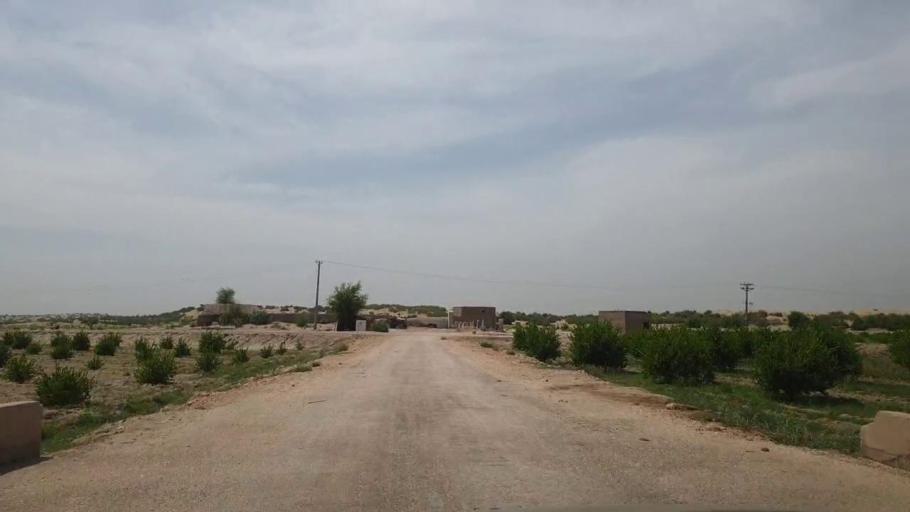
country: PK
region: Sindh
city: Bozdar
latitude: 27.0807
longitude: 69.0718
